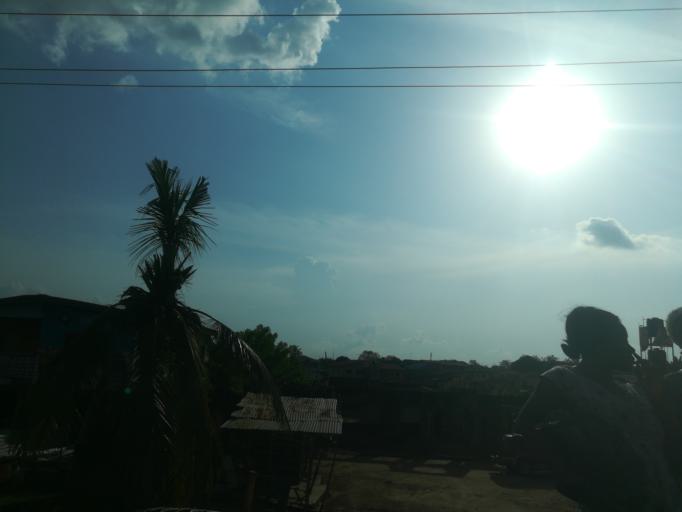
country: NG
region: Oyo
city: Ibadan
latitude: 7.3888
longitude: 3.8220
